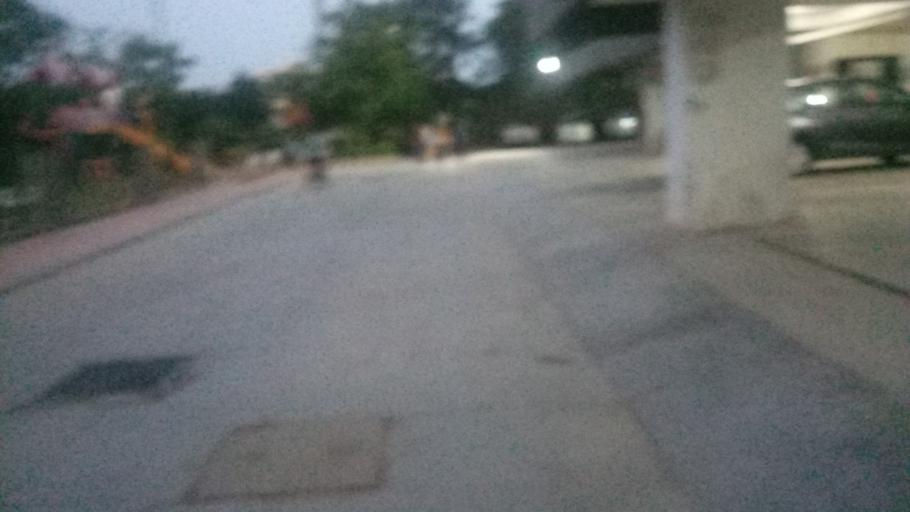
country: IN
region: Rajasthan
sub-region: Jaipur
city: Jaipur
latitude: 26.8038
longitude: 75.8685
